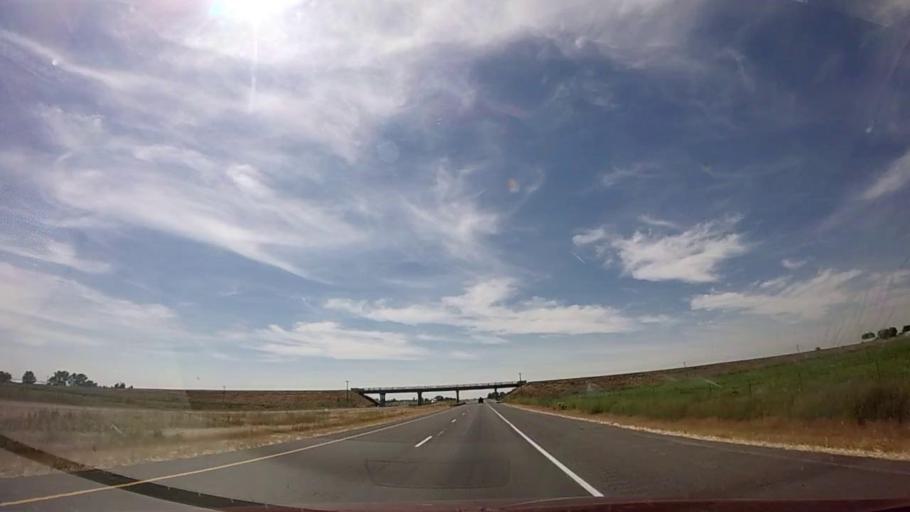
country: US
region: Idaho
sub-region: Minidoka County
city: Rupert
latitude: 42.5692
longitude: -113.6637
